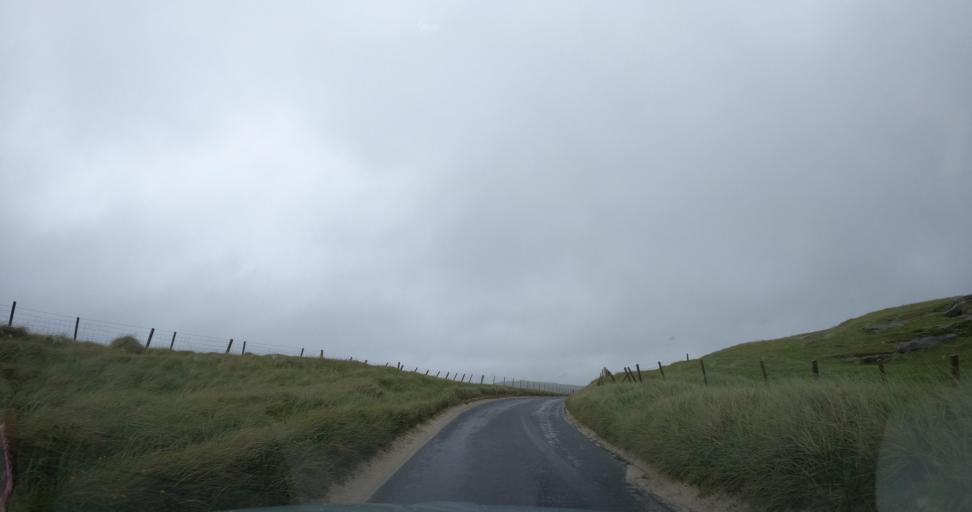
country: GB
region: Scotland
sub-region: Eilean Siar
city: Barra
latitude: 56.9947
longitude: -7.5074
